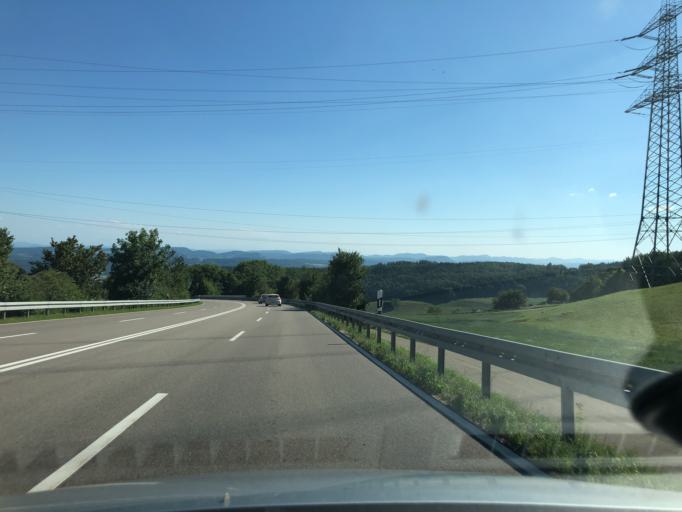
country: DE
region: Baden-Wuerttemberg
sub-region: Freiburg Region
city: Dogern
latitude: 47.6525
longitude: 8.1755
